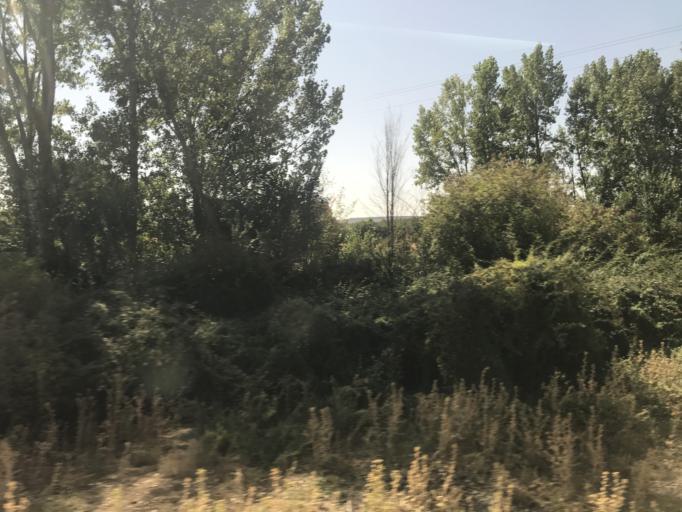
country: ES
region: Castille and Leon
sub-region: Provincia de Palencia
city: Reinoso de Cerrato
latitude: 41.9863
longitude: -4.4159
